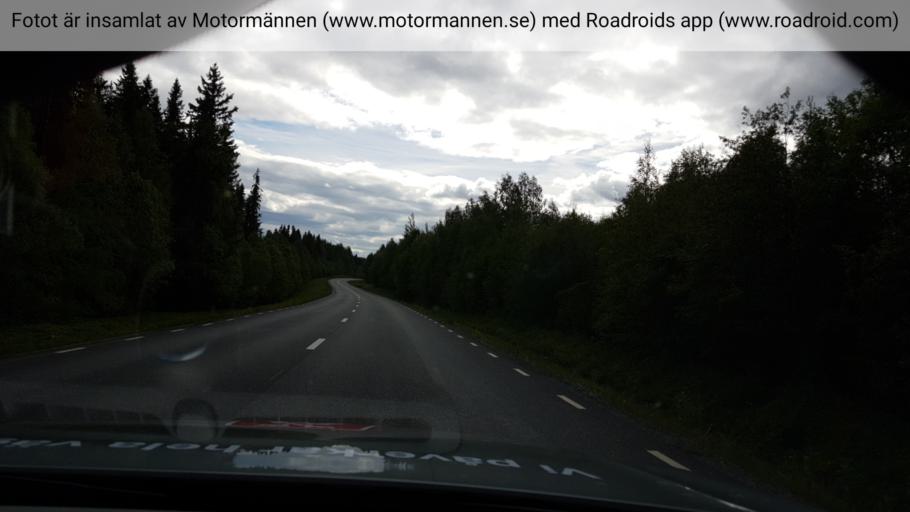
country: SE
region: Jaemtland
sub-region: Stroemsunds Kommun
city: Stroemsund
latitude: 64.1080
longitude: 15.6012
